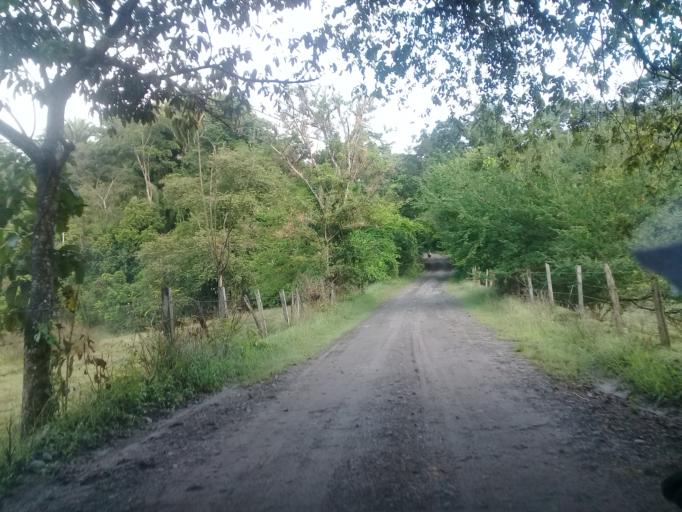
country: CO
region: Antioquia
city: Puerto Triunfo
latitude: 5.7287
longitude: -74.4713
